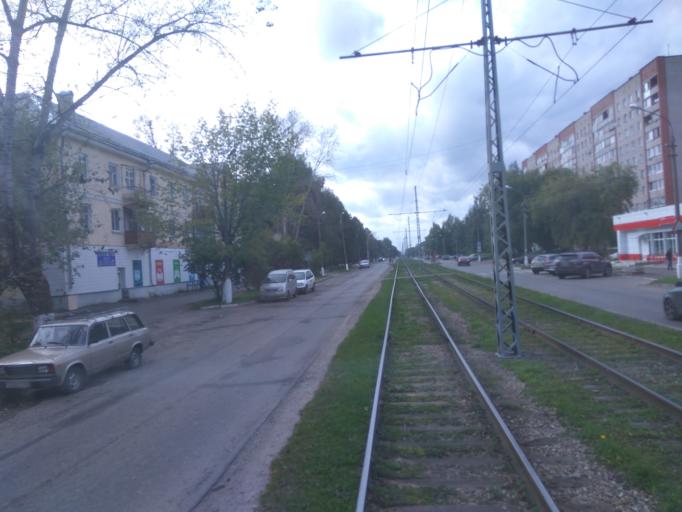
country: RU
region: Moskovskaya
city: Kolomna
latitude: 55.0765
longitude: 38.7770
